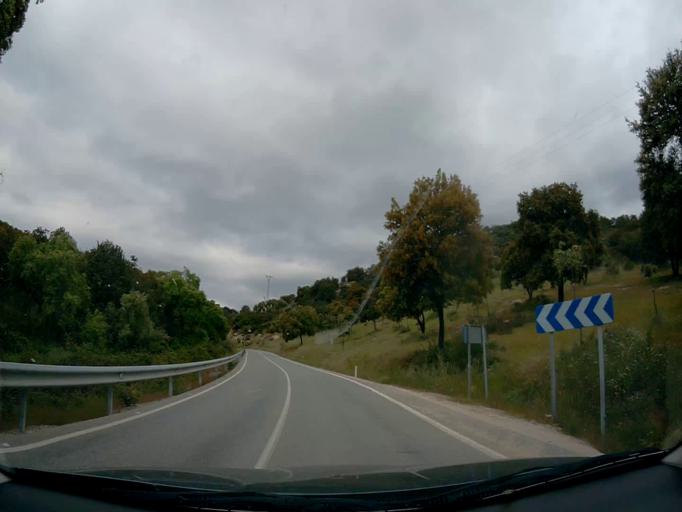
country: ES
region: Madrid
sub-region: Provincia de Madrid
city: Navalagamella
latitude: 40.4391
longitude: -4.1109
